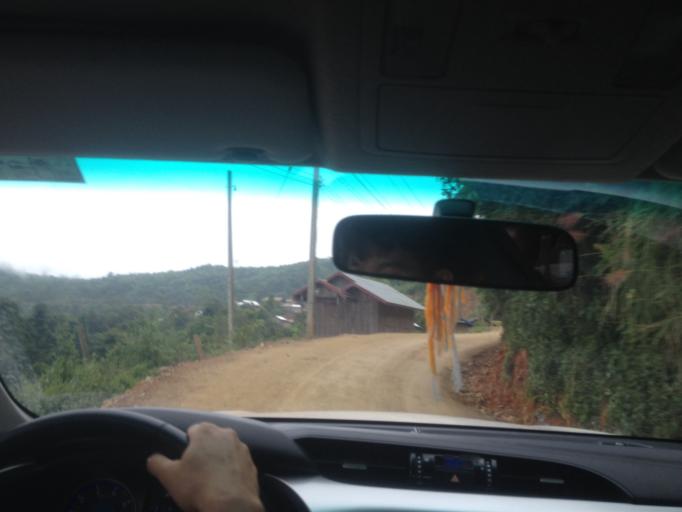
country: TH
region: Nan
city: Chaloem Phra Kiat
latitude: 19.9815
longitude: 101.1433
